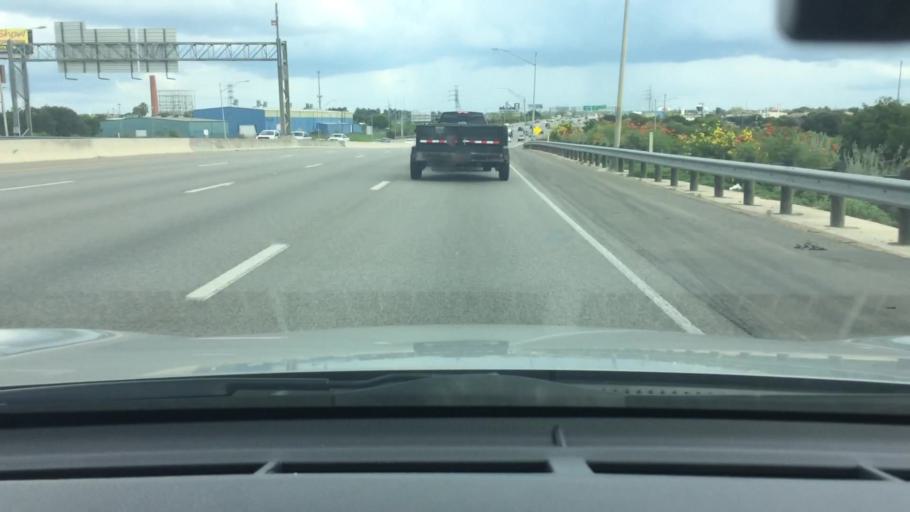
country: US
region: Texas
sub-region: Bexar County
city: San Antonio
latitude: 29.3956
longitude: -98.4972
